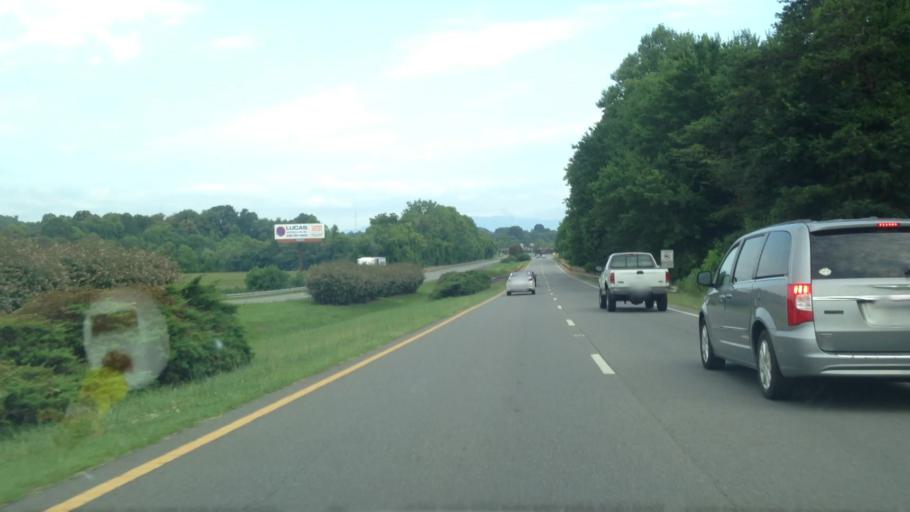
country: US
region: North Carolina
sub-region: Surry County
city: Mount Airy
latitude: 36.4816
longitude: -80.6058
